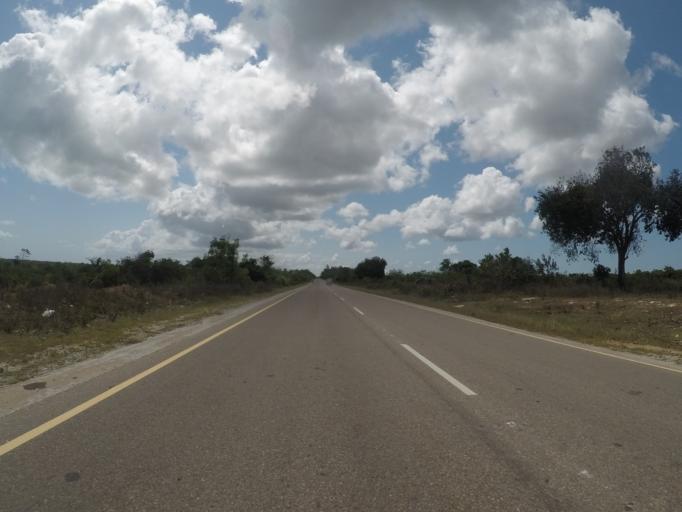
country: TZ
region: Zanzibar Central/South
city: Koani
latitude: -6.2659
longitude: 39.3610
